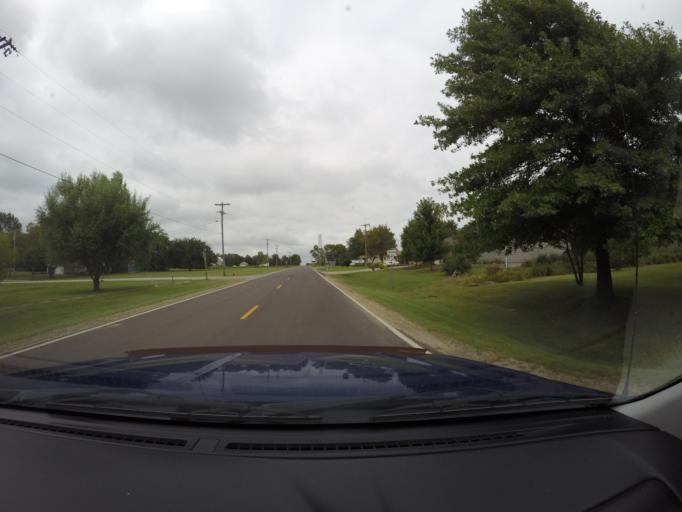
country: US
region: Kansas
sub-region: Morris County
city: Council Grove
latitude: 38.8475
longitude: -96.5940
